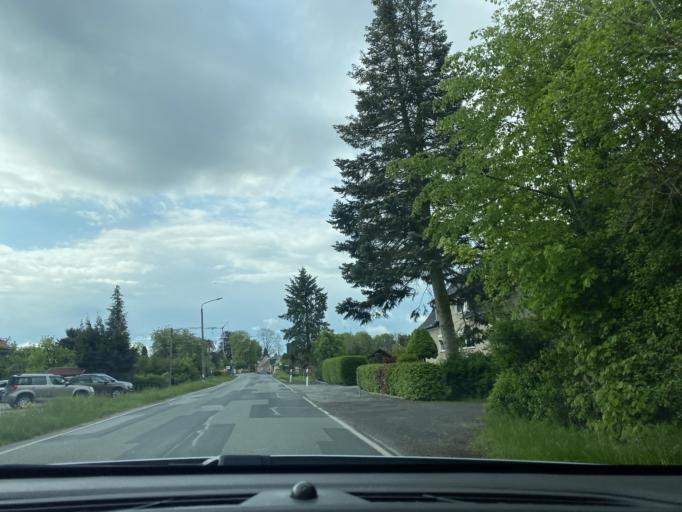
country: DE
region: Saxony
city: Horka
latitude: 51.2900
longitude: 14.8926
